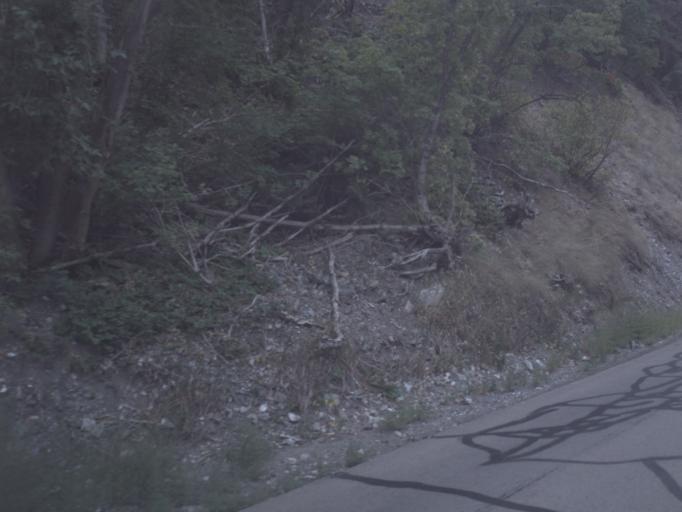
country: US
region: Utah
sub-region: Utah County
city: Cedar Hills
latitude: 40.4371
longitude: -111.7258
